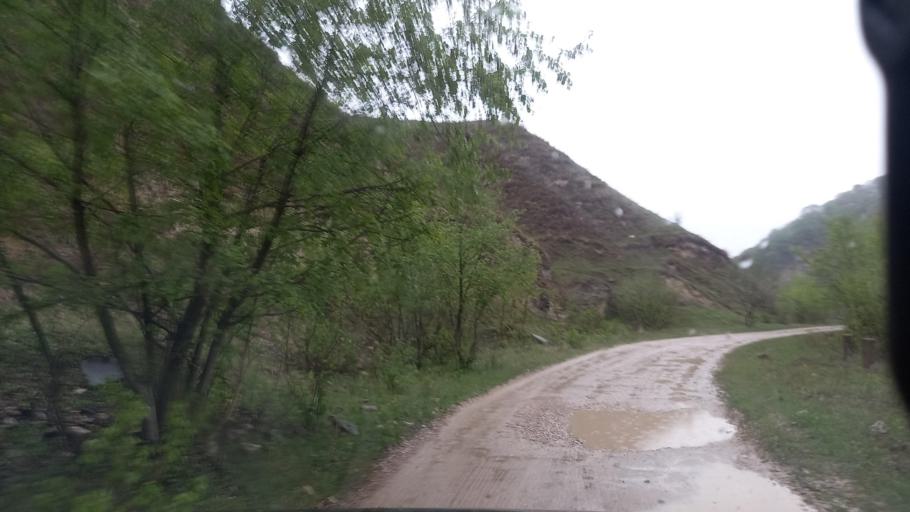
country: RU
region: Kabardino-Balkariya
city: Bylym
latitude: 43.5906
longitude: 43.0231
